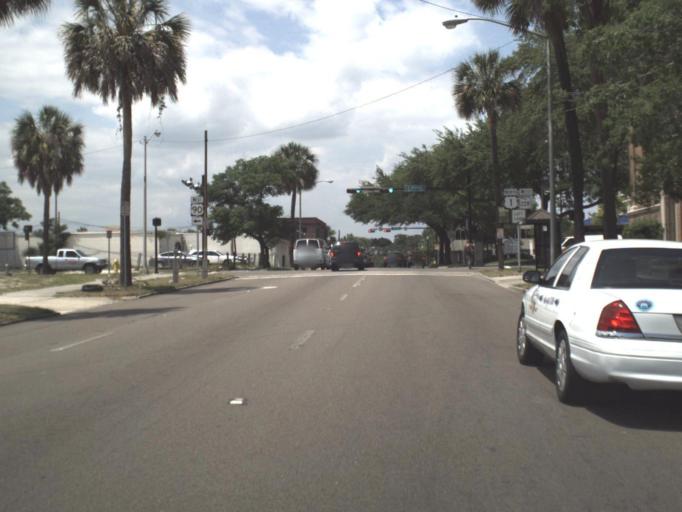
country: US
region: Florida
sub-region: Duval County
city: Jacksonville
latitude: 30.3307
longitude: -81.6554
